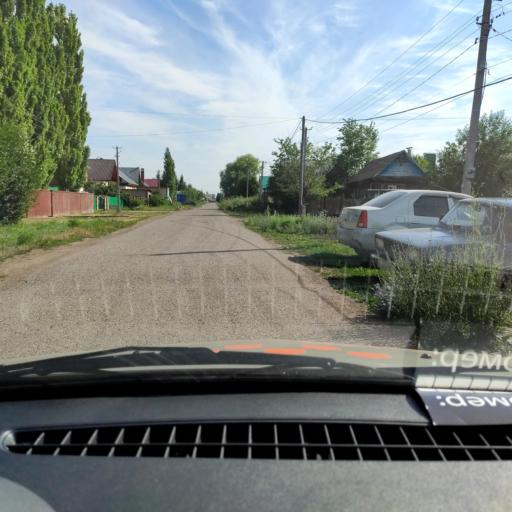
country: RU
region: Bashkortostan
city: Ufa
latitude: 54.6109
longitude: 55.8949
